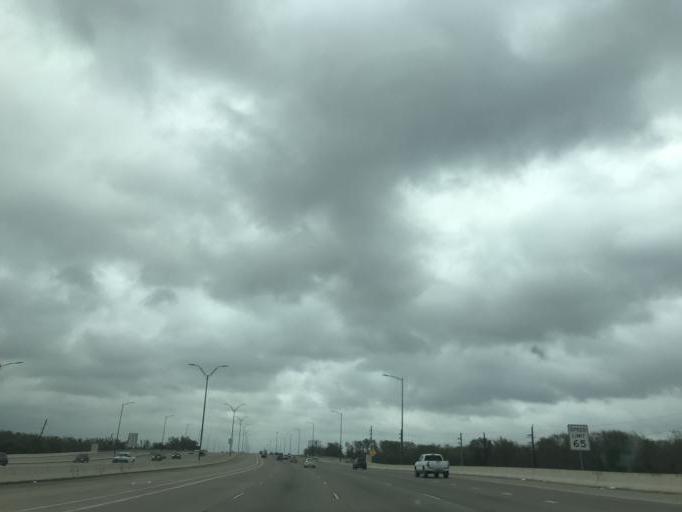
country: US
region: Texas
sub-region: Fort Bend County
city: Greatwood
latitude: 29.5657
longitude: -95.6720
